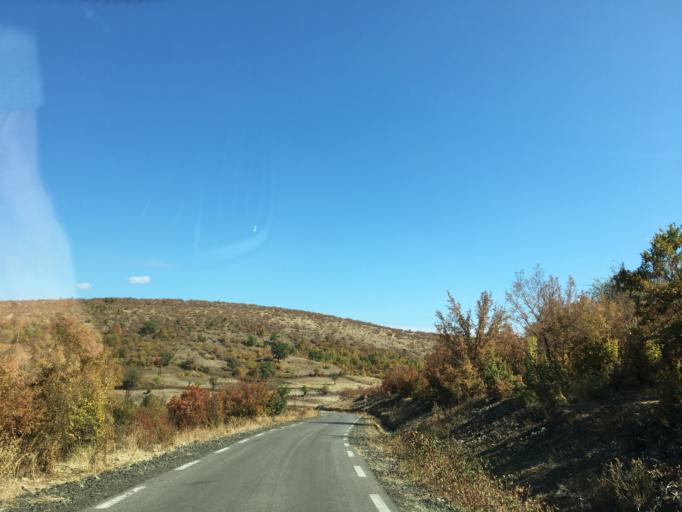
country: BG
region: Kurdzhali
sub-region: Obshtina Krumovgrad
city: Krumovgrad
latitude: 41.5142
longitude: 25.5318
